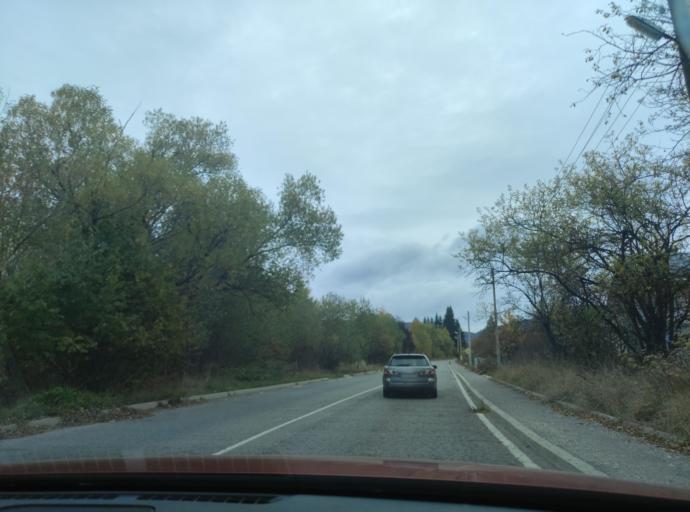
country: BG
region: Sofiya
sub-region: Obshtina Godech
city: Godech
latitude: 43.0911
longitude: 23.0980
